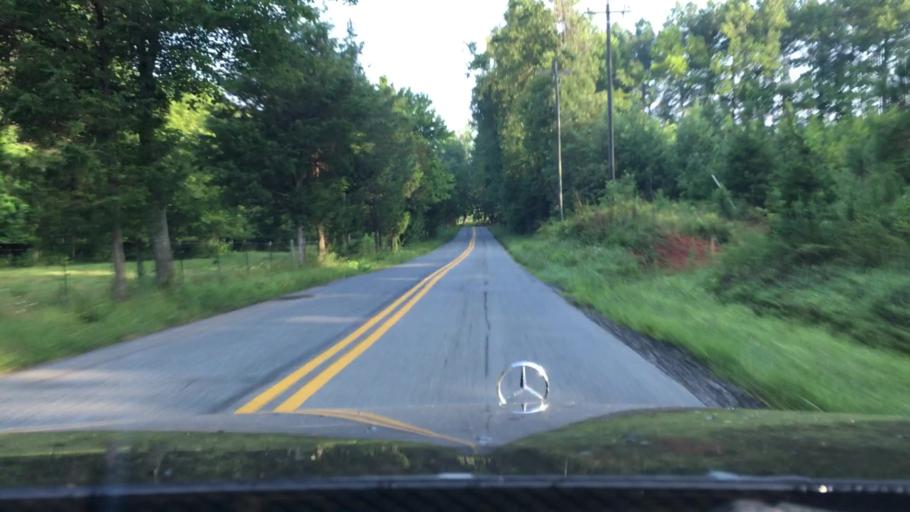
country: US
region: Virginia
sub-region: Campbell County
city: Timberlake
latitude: 37.2797
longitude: -79.2698
